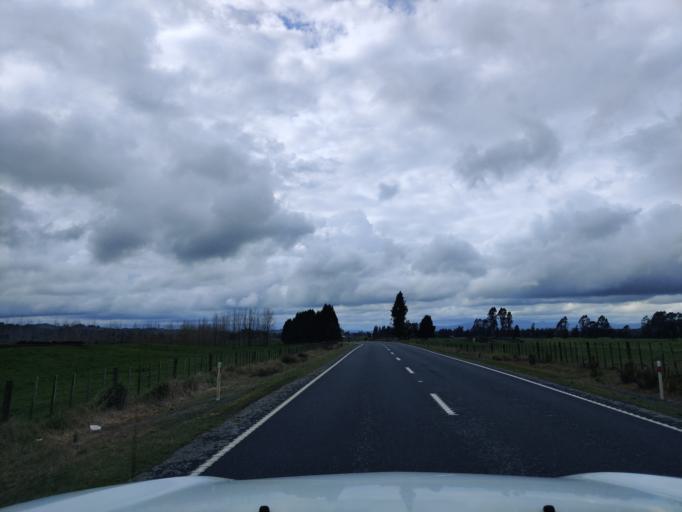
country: NZ
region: Waikato
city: Turangi
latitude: -39.0369
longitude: 175.3830
